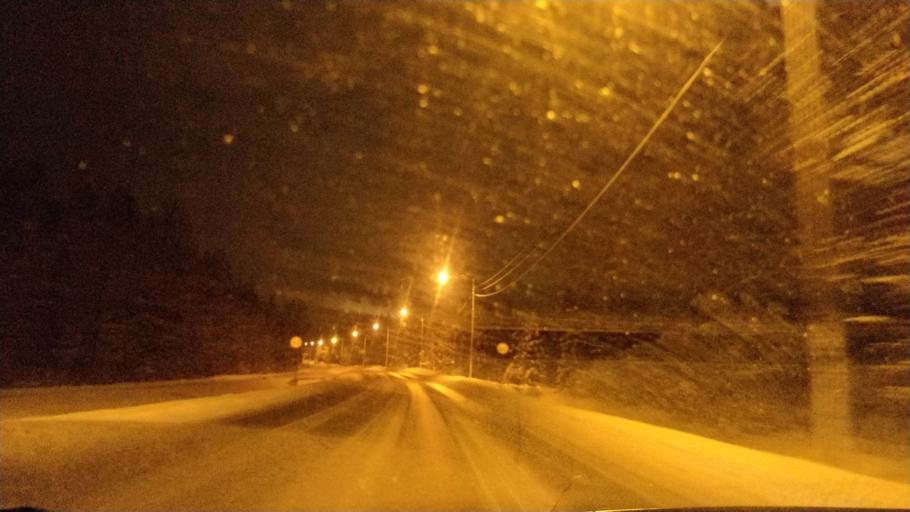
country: FI
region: Lapland
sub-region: Rovaniemi
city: Rovaniemi
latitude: 66.3859
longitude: 25.3769
